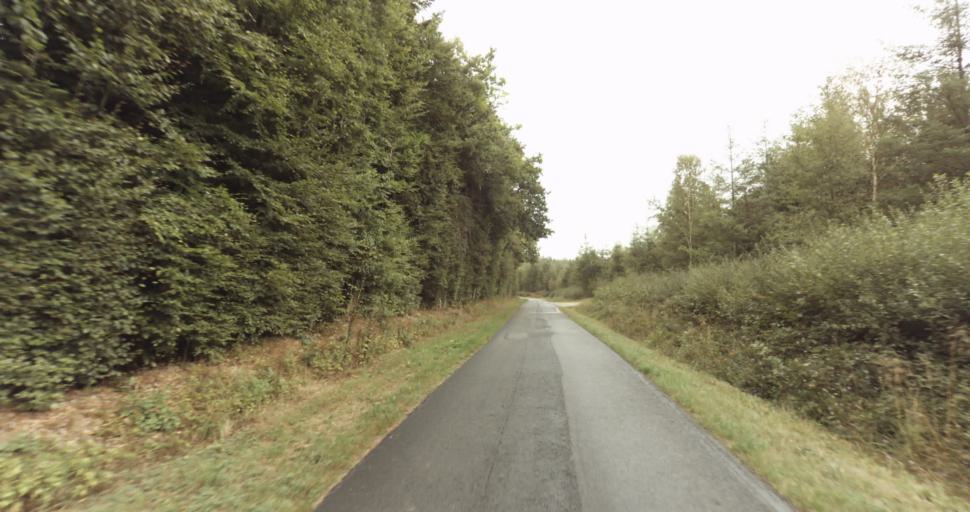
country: FR
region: Lower Normandy
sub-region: Departement de l'Orne
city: Gace
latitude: 48.8179
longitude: 0.3401
